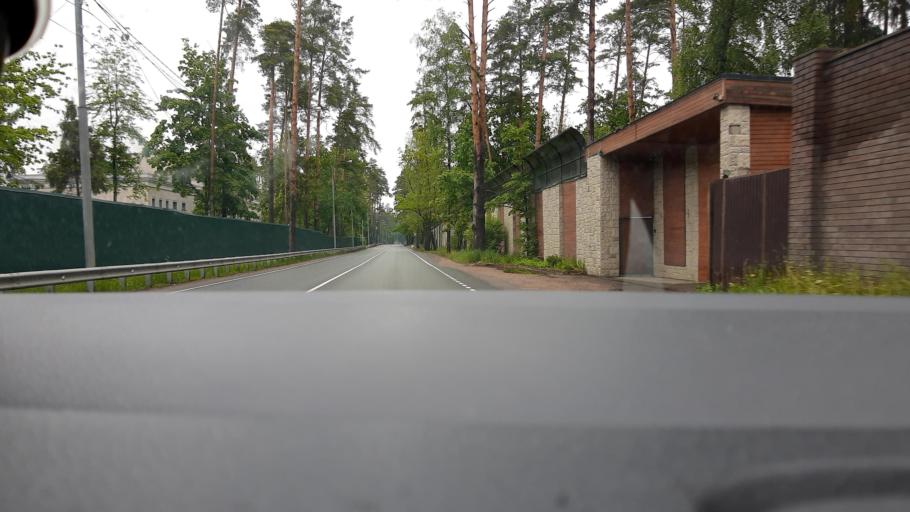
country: RU
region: Moskovskaya
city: Nazar'yevo
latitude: 55.7007
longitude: 37.0632
